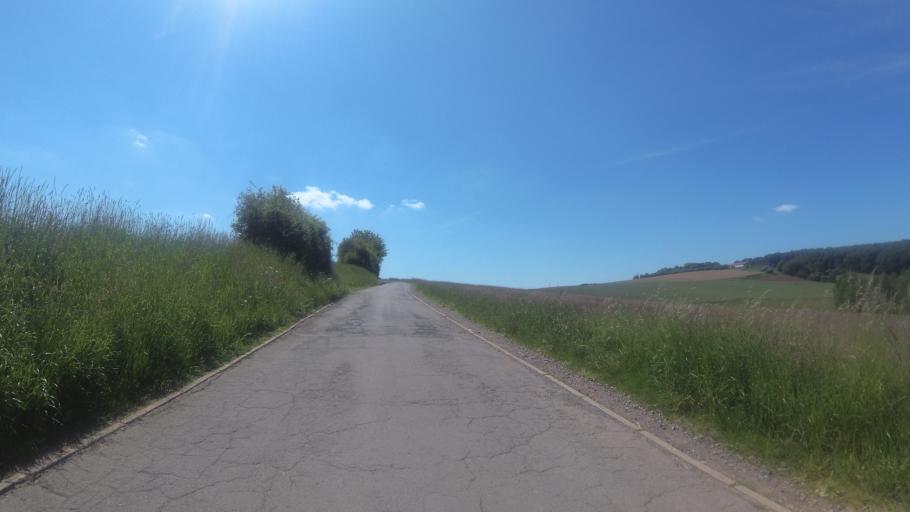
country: DE
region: Saarland
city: Heusweiler
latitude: 49.3499
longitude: 6.9172
